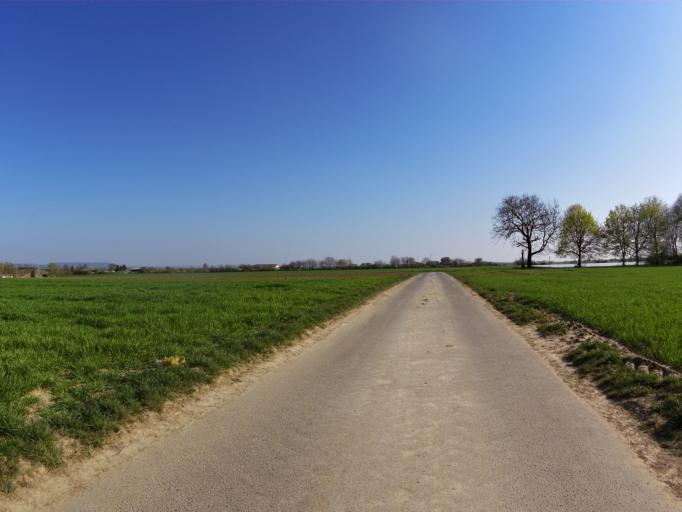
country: DE
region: Bavaria
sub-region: Regierungsbezirk Unterfranken
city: Oberpleichfeld
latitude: 49.8256
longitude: 10.0909
